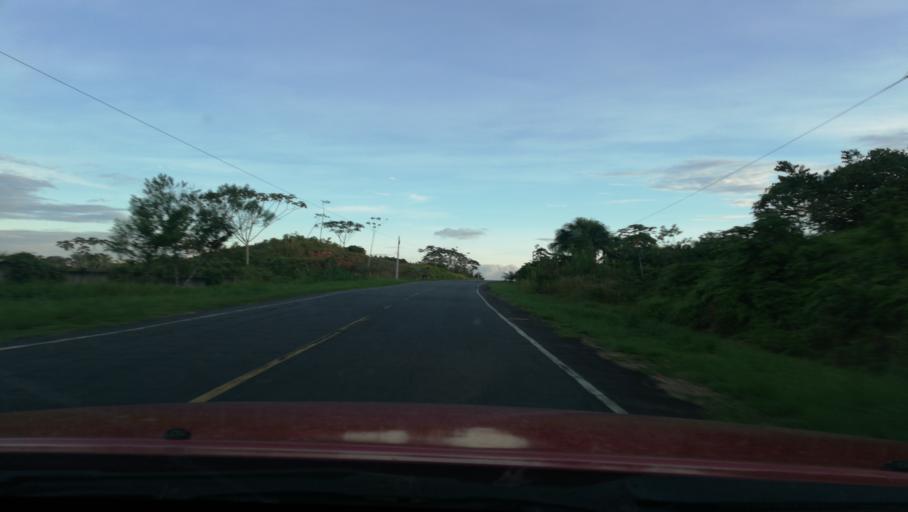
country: PE
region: Loreto
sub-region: Provincia de Loreto
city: Nauta
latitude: -4.2745
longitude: -73.5126
